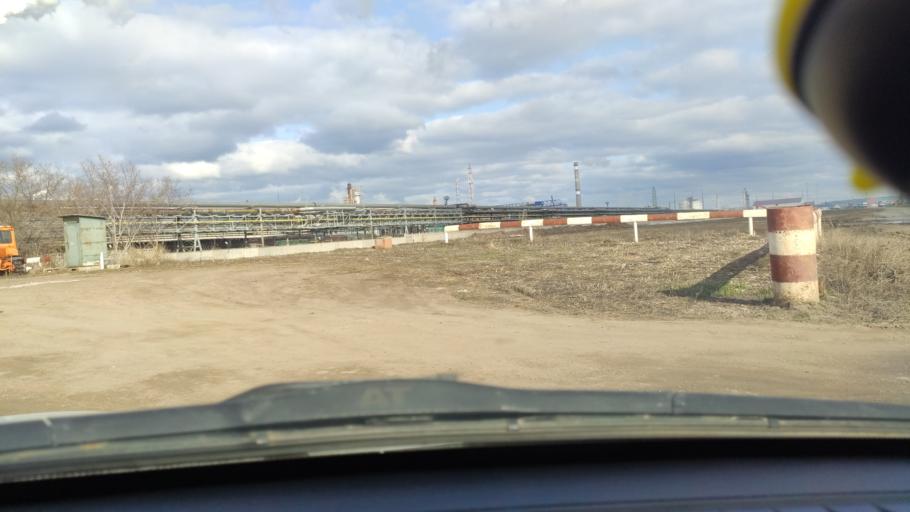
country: RU
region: Samara
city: Tol'yatti
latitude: 53.5486
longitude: 49.4638
